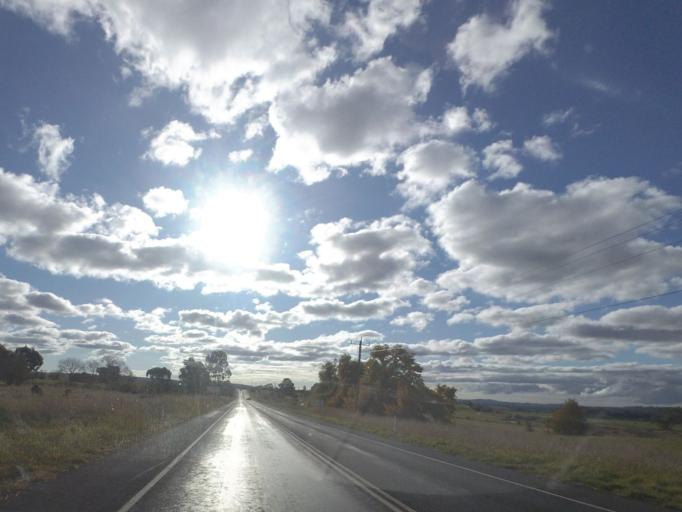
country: AU
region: Victoria
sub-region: Mount Alexander
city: Castlemaine
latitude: -37.1827
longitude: 144.3636
